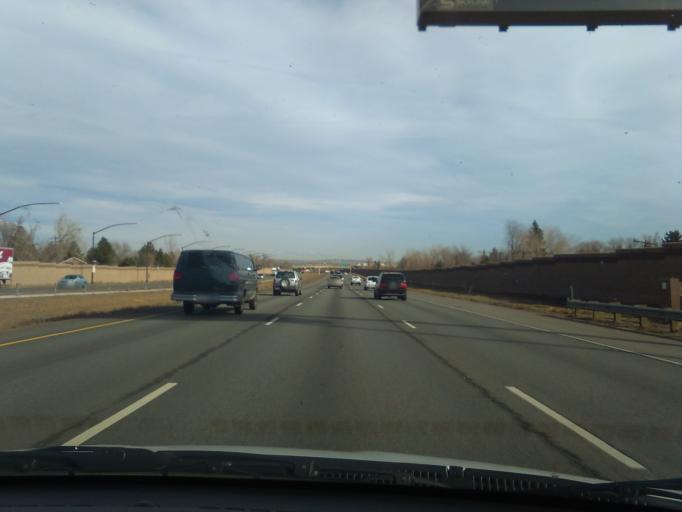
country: US
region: Colorado
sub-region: Jefferson County
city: Applewood
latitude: 39.7498
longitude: -105.1488
